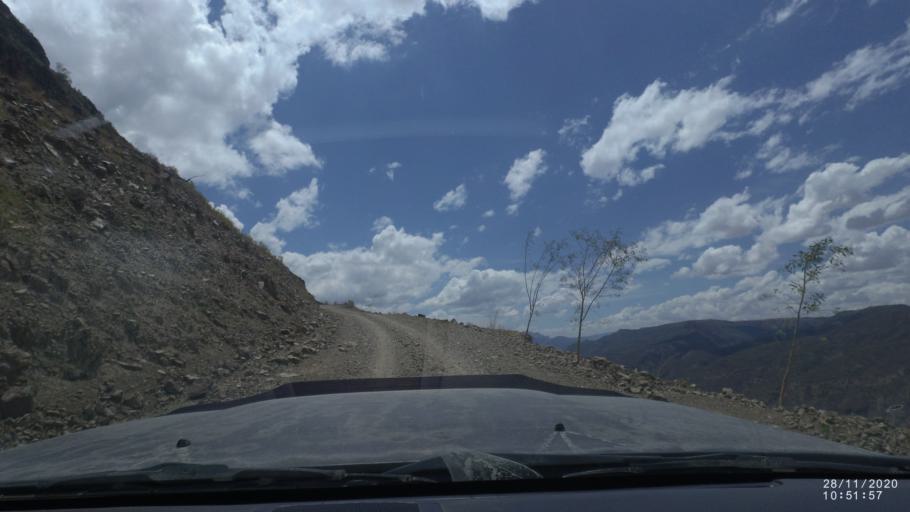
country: BO
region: Cochabamba
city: Capinota
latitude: -17.7852
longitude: -66.1221
